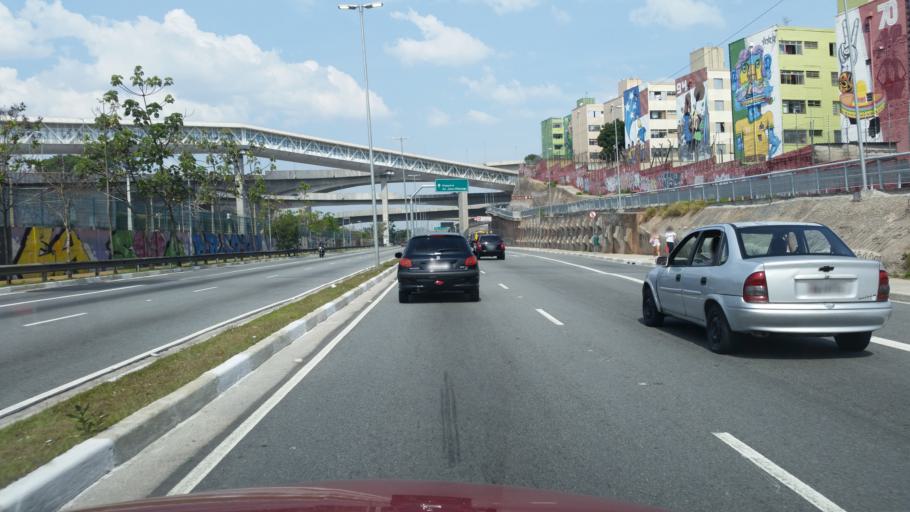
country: BR
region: Sao Paulo
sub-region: Guarulhos
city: Guarulhos
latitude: -23.5422
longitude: -46.4814
